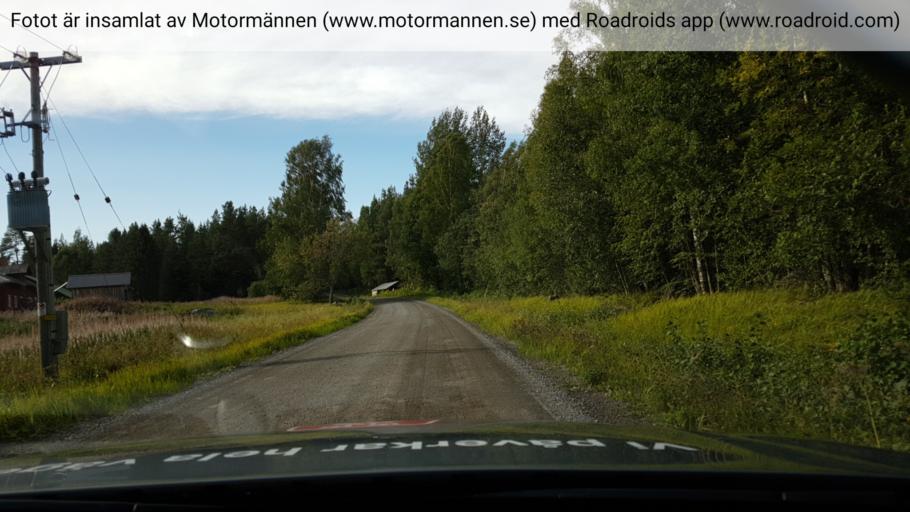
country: SE
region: Jaemtland
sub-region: Braecke Kommun
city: Braecke
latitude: 63.2068
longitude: 15.4031
